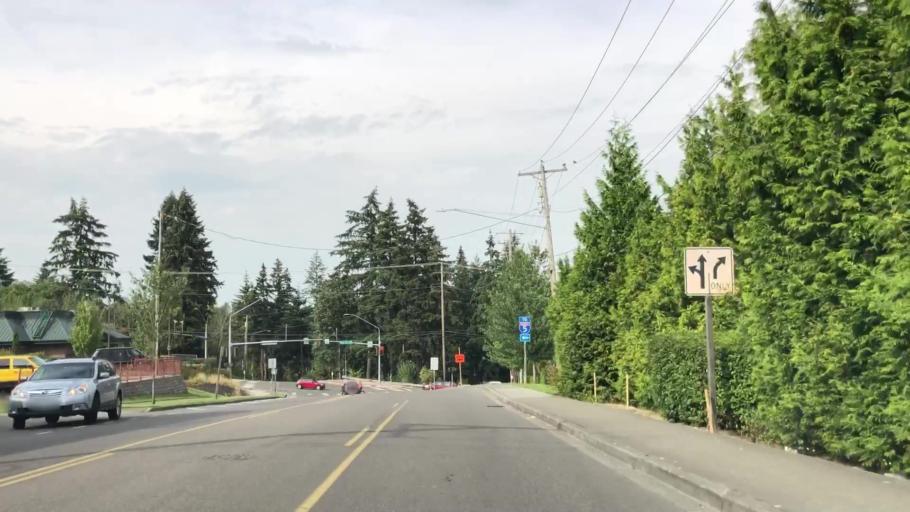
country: US
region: Washington
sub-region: Snohomish County
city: Martha Lake
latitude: 47.8484
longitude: -122.2467
